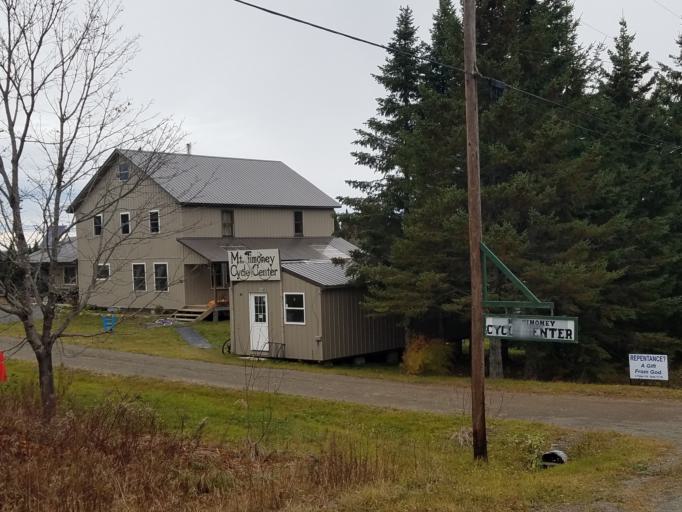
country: US
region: Maine
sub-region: Aroostook County
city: Hodgdon
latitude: 46.1323
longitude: -68.1139
